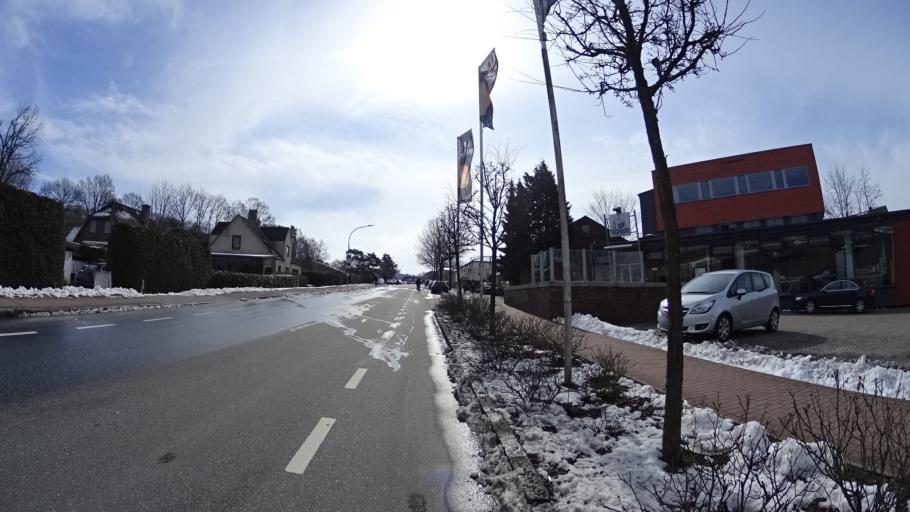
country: DE
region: Schleswig-Holstein
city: Boostedt
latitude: 54.0118
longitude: 10.0241
